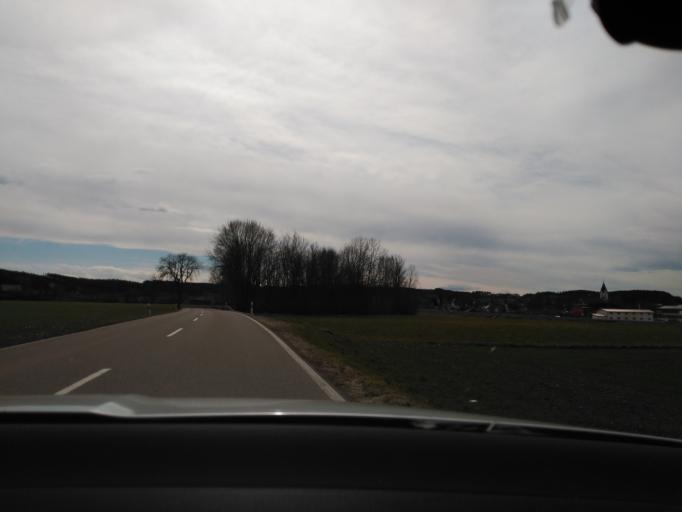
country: DE
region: Baden-Wuerttemberg
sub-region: Tuebingen Region
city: Aichstetten
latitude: 47.9006
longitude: 10.0876
